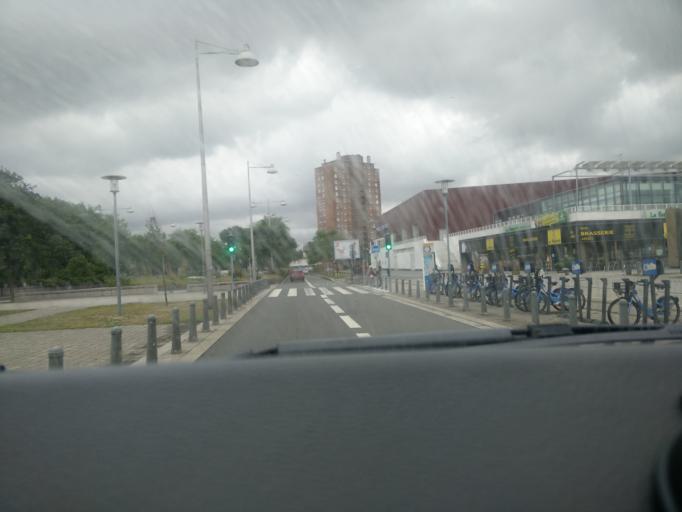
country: FR
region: Nord-Pas-de-Calais
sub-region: Departement du Nord
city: Dunkerque
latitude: 51.0346
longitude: 2.3723
